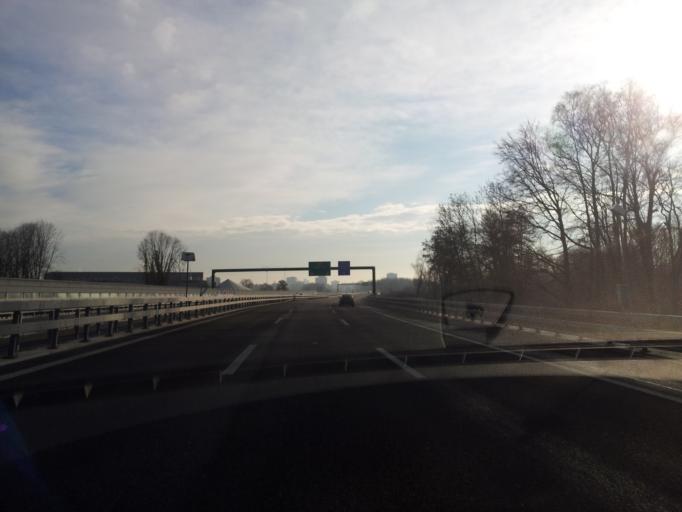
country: CH
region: Zurich
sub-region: Bezirk Dietikon
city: Oberengstringen
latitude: 47.4032
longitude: 8.4687
